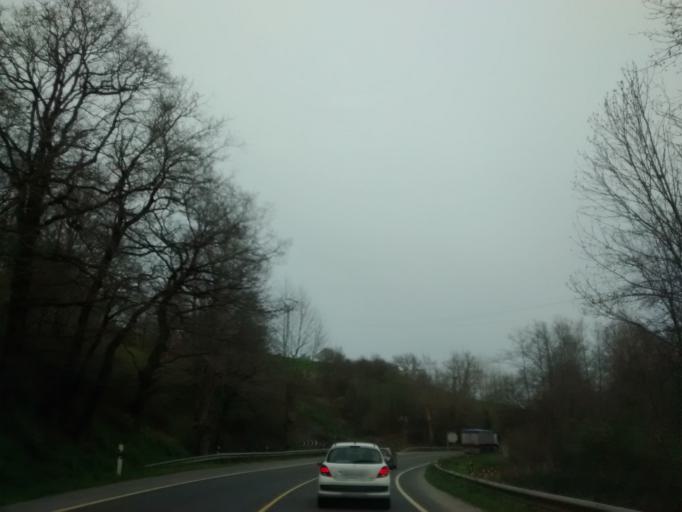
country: ES
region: Cantabria
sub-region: Provincia de Cantabria
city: Penagos
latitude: 43.3493
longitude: -3.7857
